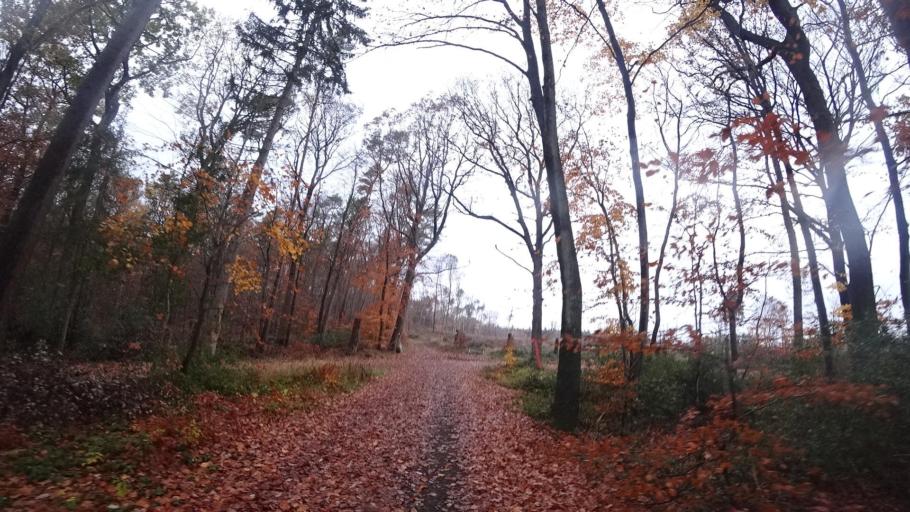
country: DE
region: Rheinland-Pfalz
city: Schalkenbach
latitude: 50.5119
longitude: 7.1294
